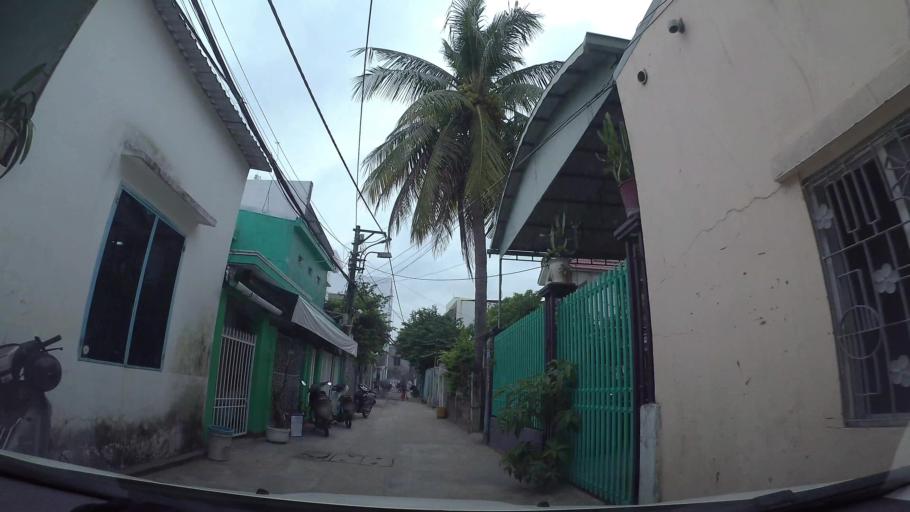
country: VN
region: Da Nang
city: Son Tra
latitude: 16.0607
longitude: 108.2382
